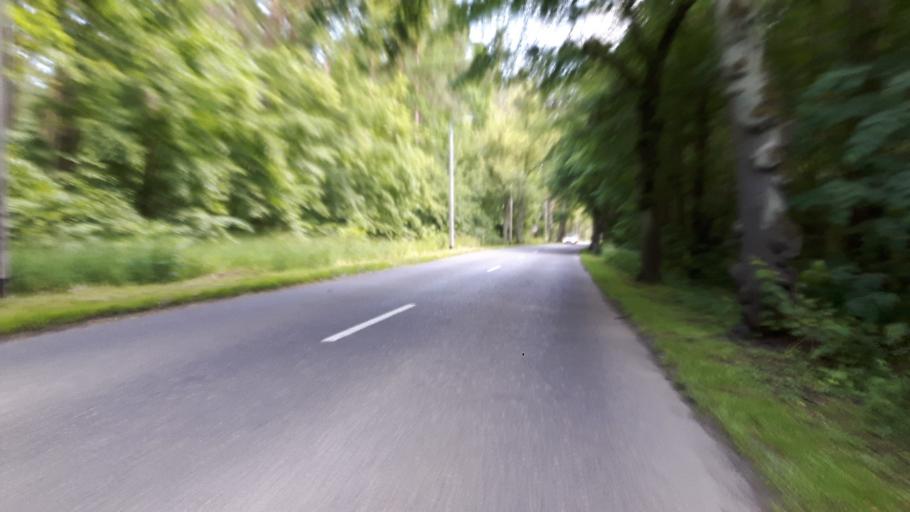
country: PL
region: Pomeranian Voivodeship
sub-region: Powiat gdanski
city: Cedry Wielkie
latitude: 54.3405
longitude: 18.8837
